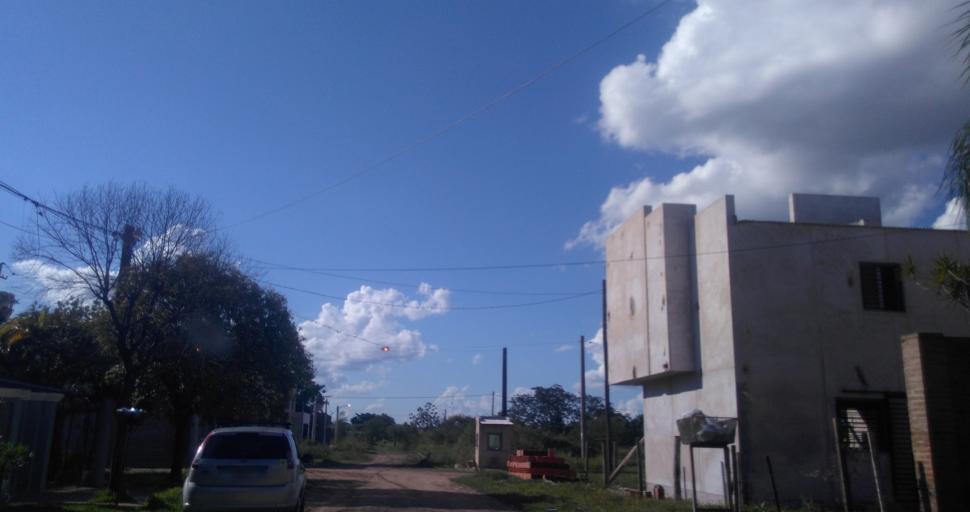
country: AR
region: Chaco
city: Resistencia
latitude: -27.4363
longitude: -58.9641
